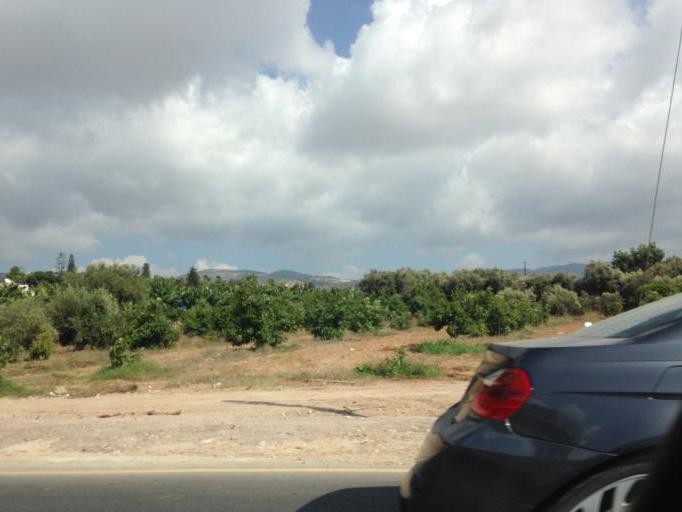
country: CY
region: Pafos
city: Pegeia
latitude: 34.8624
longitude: 32.3799
